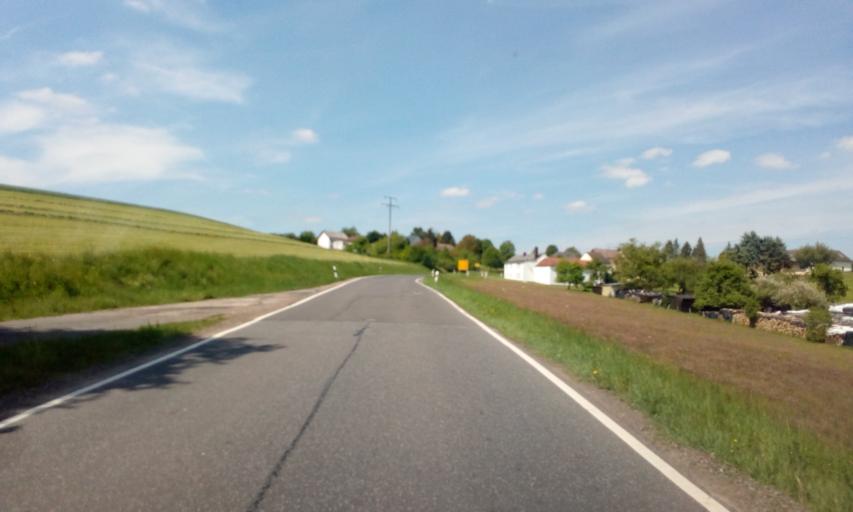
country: DE
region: Rheinland-Pfalz
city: Niedergeckler
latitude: 49.9667
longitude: 6.2967
